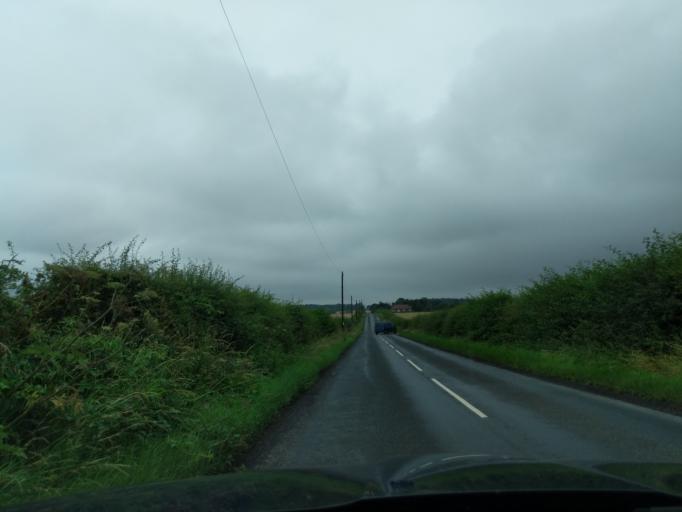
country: GB
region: England
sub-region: Northumberland
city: Ford
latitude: 55.6654
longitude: -2.1017
